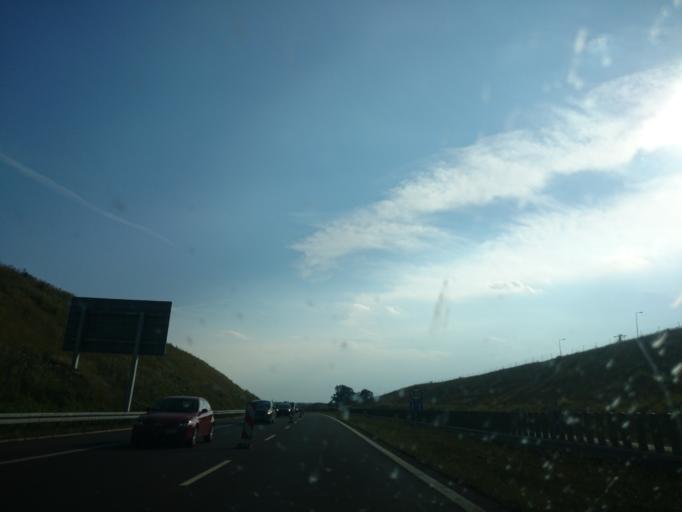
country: PL
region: Silesian Voivodeship
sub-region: Powiat rybnicki
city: Swierklany Dolne
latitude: 50.0130
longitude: 18.5888
